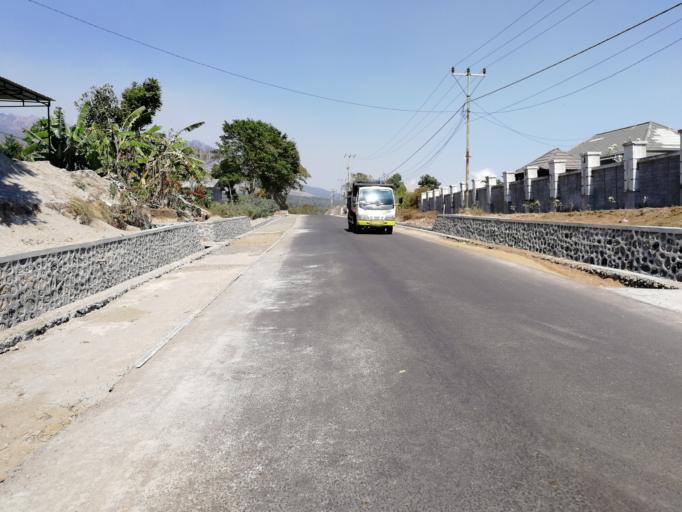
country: ID
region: West Nusa Tenggara
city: Sembalunlawang
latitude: -8.3576
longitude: 116.5172
